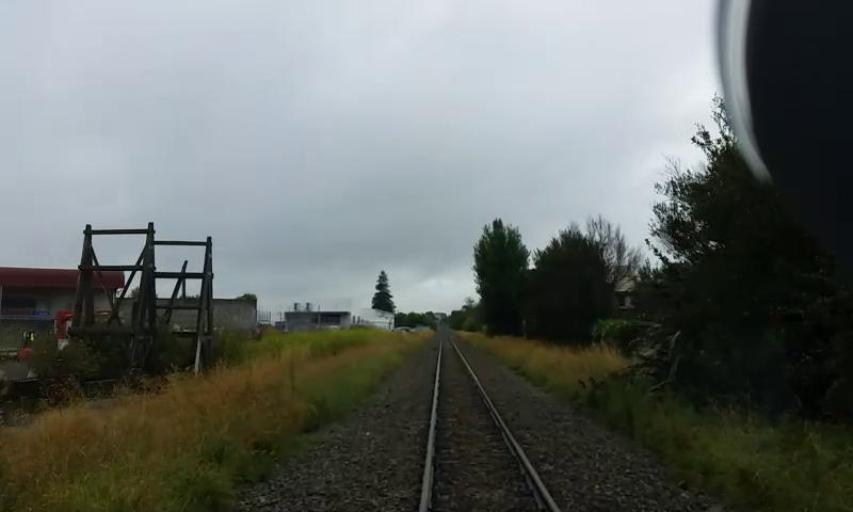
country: NZ
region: Canterbury
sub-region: Christchurch City
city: Christchurch
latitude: -43.5334
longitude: 172.6093
